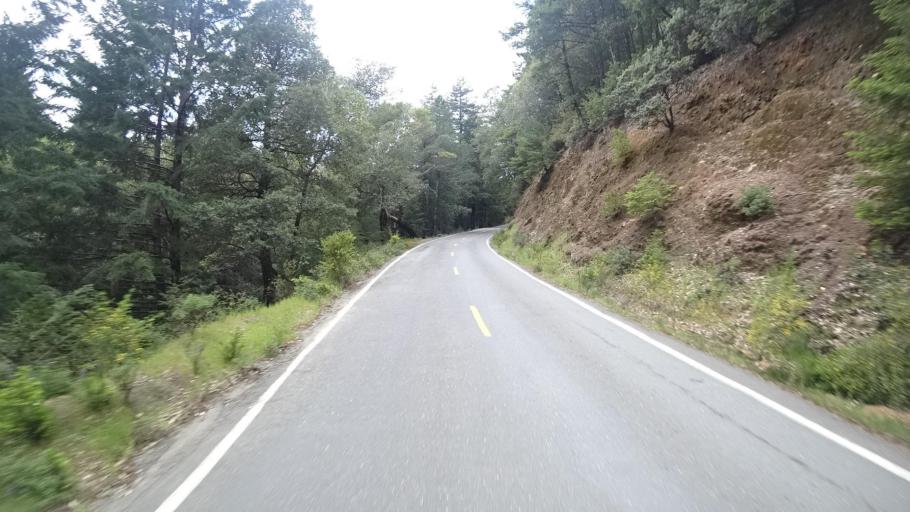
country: US
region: California
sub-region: Humboldt County
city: Redway
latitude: 40.0395
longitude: -124.0217
